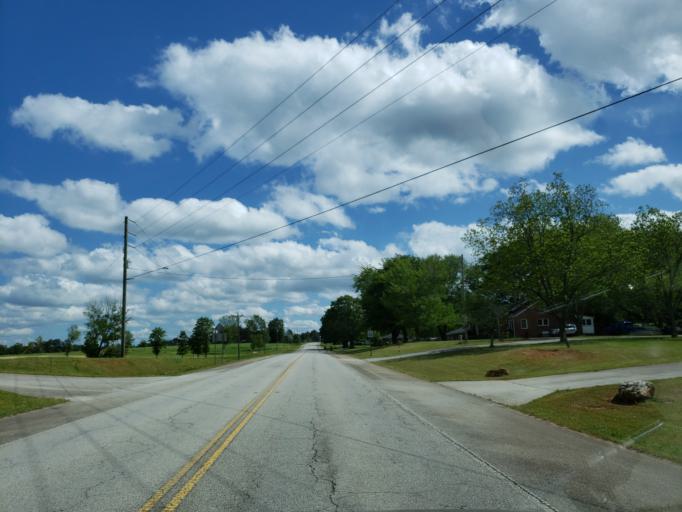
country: US
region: Georgia
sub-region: Haralson County
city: Bremen
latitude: 33.7365
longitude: -85.1133
